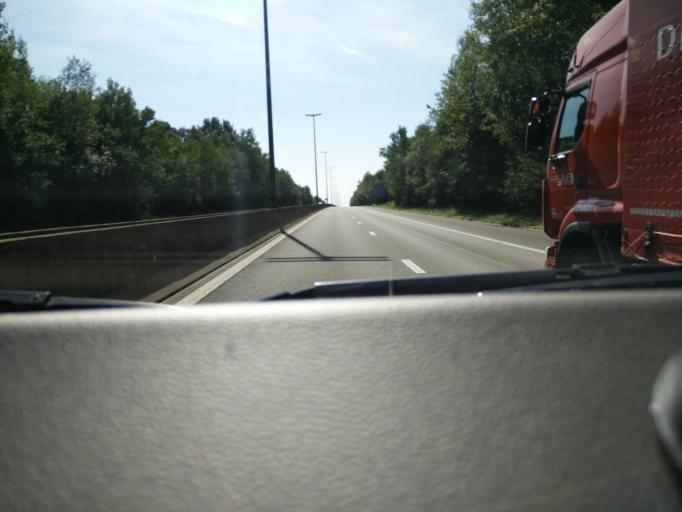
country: BE
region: Wallonia
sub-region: Province du Luxembourg
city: Leglise
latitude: 49.7612
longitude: 5.5612
